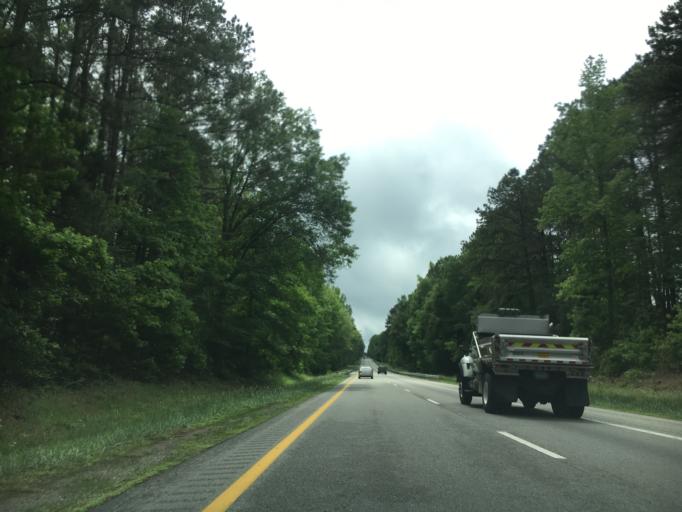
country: US
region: Virginia
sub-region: Brunswick County
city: Lawrenceville
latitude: 36.8610
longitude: -77.8448
